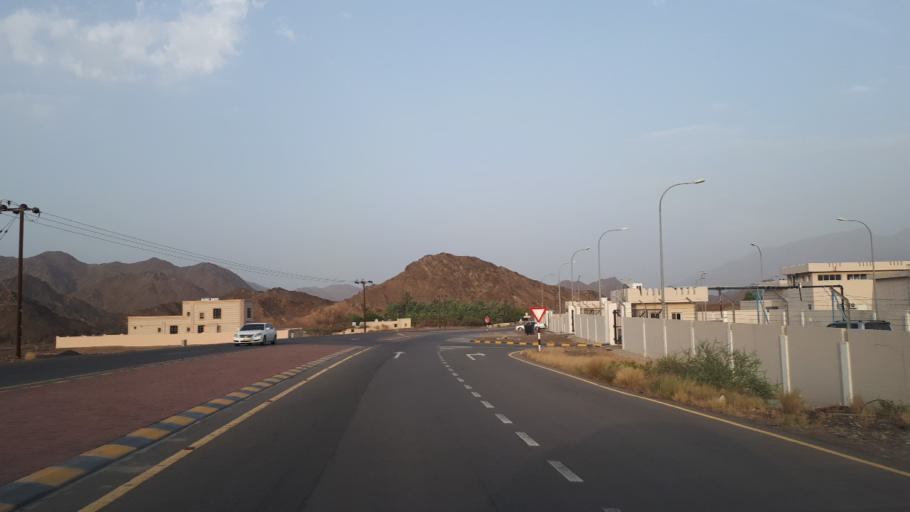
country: OM
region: Al Batinah
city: Rustaq
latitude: 23.4306
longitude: 57.2777
